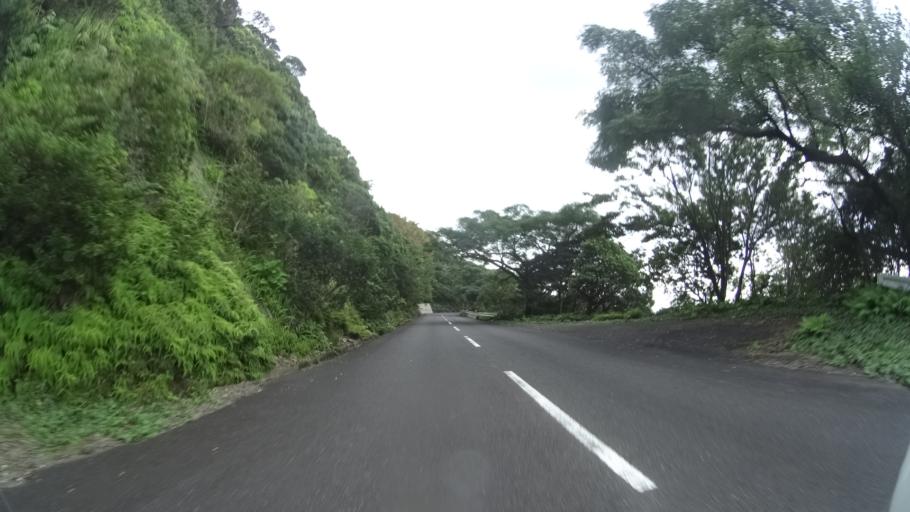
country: JP
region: Kagoshima
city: Nishinoomote
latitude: 30.3124
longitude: 130.4062
